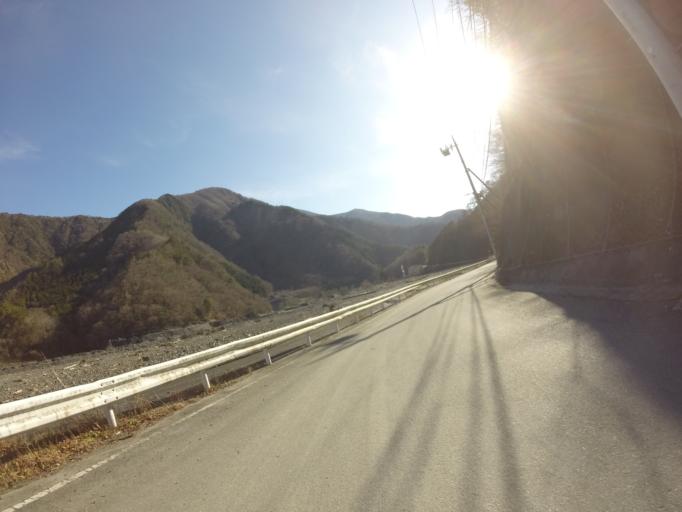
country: JP
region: Yamanashi
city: Ryuo
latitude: 35.4039
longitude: 138.3269
